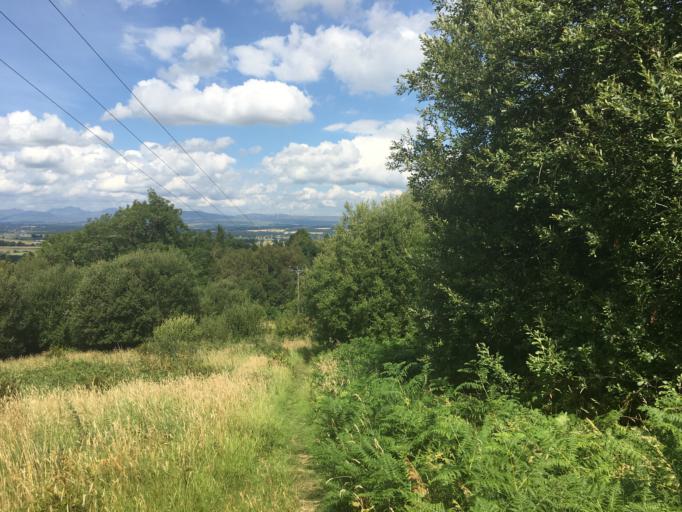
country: GB
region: Scotland
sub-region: Stirling
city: Stirling
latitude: 56.1032
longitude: -3.9831
